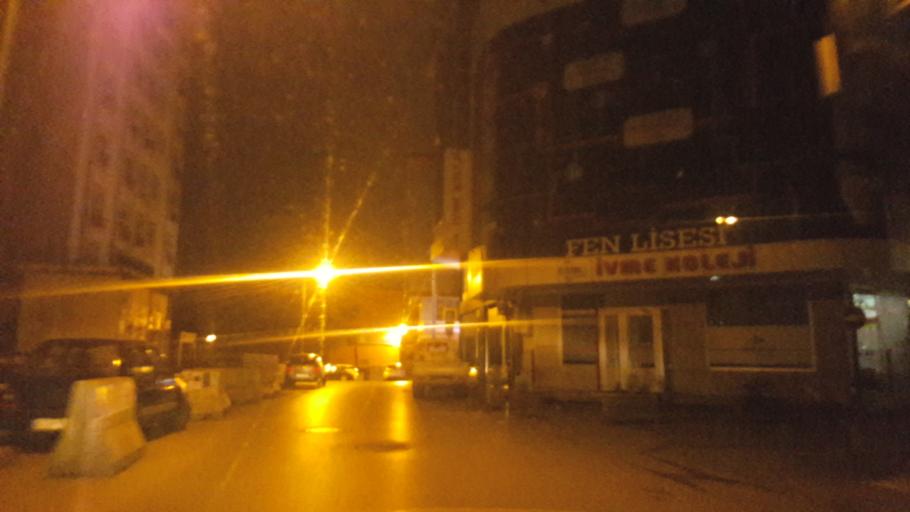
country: TR
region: Kocaeli
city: Gebze
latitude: 40.7973
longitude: 29.4366
